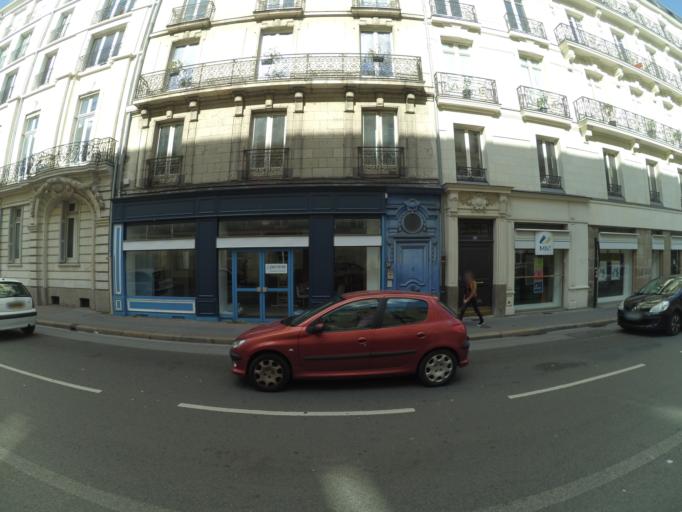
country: FR
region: Pays de la Loire
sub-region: Departement de la Loire-Atlantique
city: Nantes
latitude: 47.2176
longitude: -1.5526
